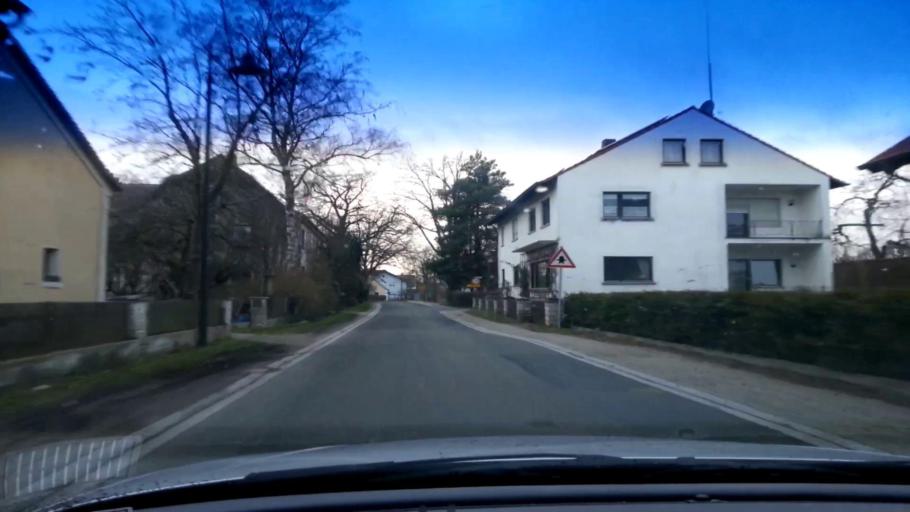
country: DE
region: Bavaria
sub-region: Upper Franconia
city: Frensdorf
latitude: 49.8240
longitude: 10.8403
